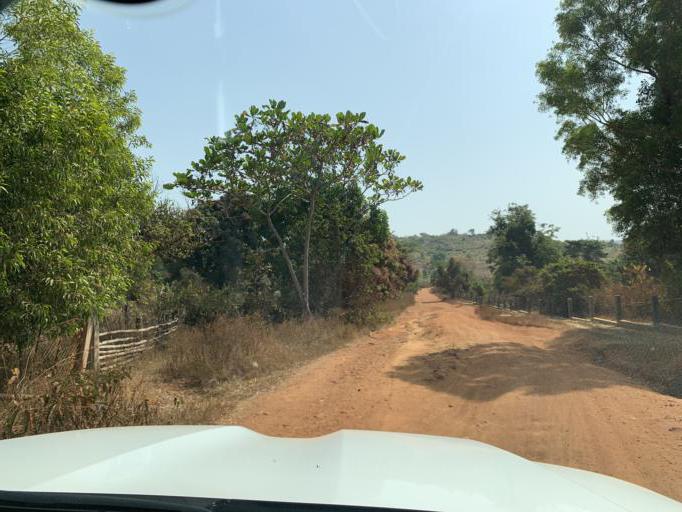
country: GN
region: Mamou
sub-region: Dalaba
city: Dalaba
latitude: 10.7541
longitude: -12.2402
